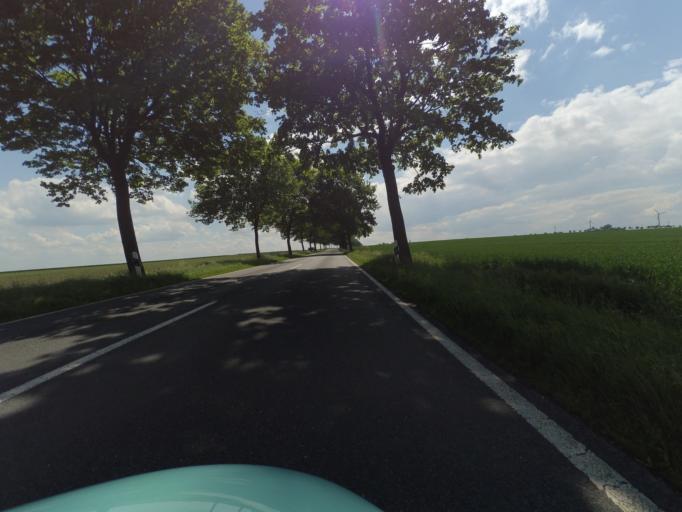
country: DE
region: Lower Saxony
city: Hohenhameln
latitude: 52.2135
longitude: 10.0364
